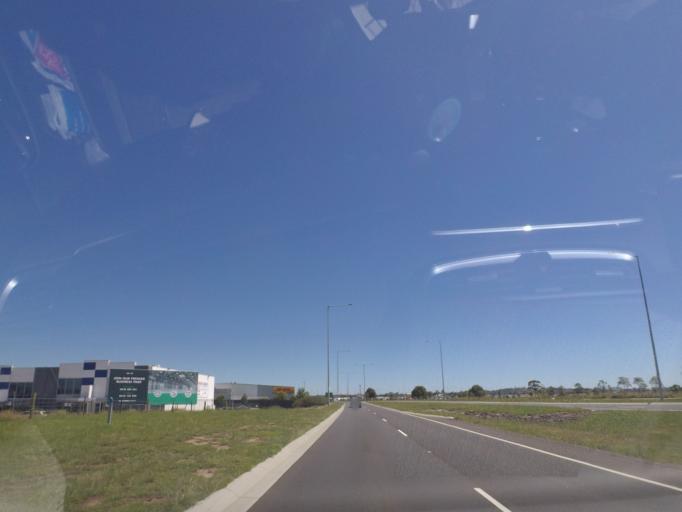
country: AU
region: Victoria
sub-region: Hume
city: Gladstone Park
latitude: -37.6853
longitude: 144.8649
